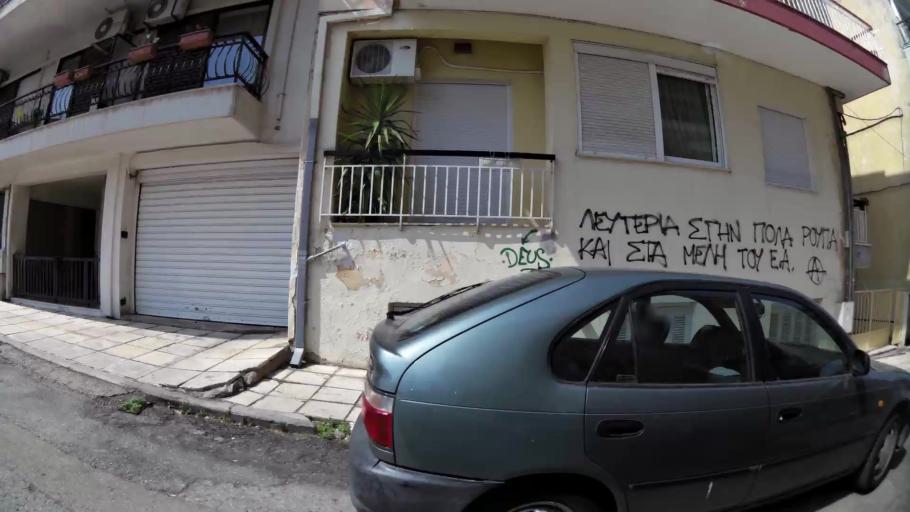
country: GR
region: Central Macedonia
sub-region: Nomos Thessalonikis
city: Thessaloniki
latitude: 40.6474
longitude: 22.9403
